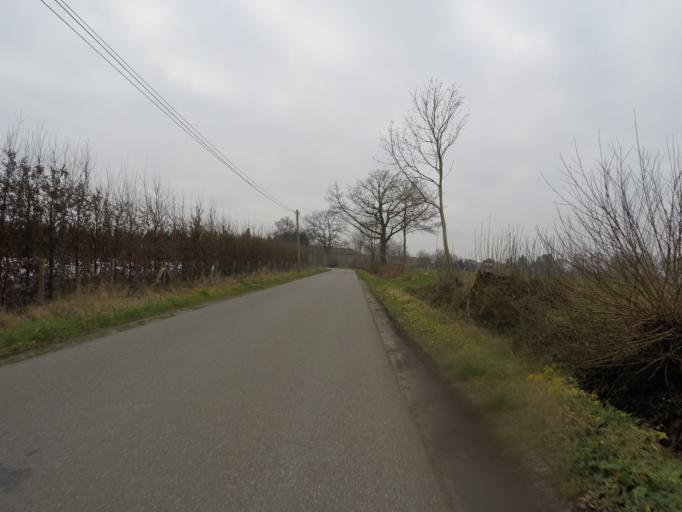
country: DE
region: Schleswig-Holstein
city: Tangstedt
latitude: 53.6877
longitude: 9.8553
